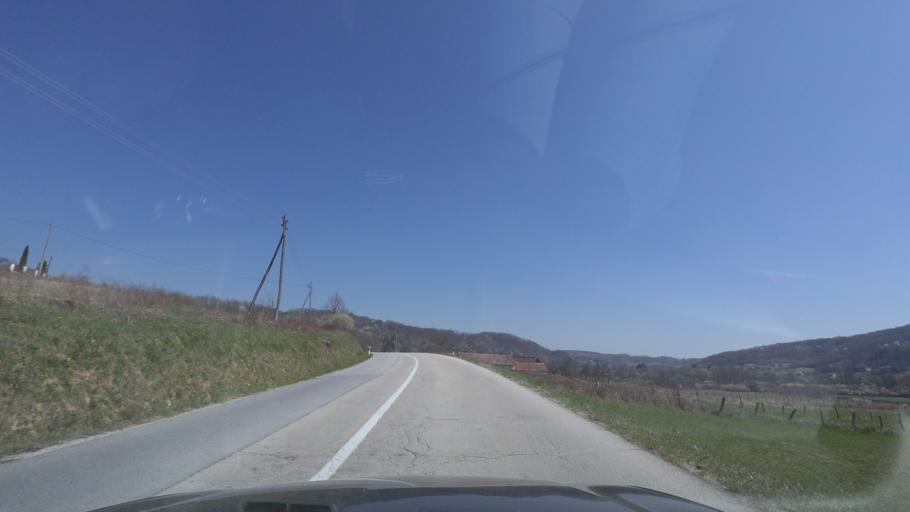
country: HR
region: Karlovacka
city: Vojnic
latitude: 45.3769
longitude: 15.6285
